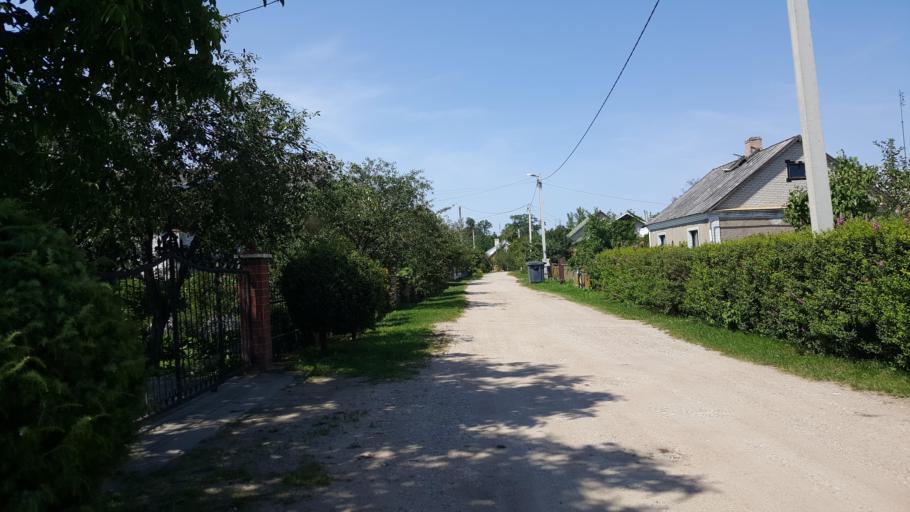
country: BY
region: Brest
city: Vysokaye
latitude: 52.3672
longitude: 23.3740
